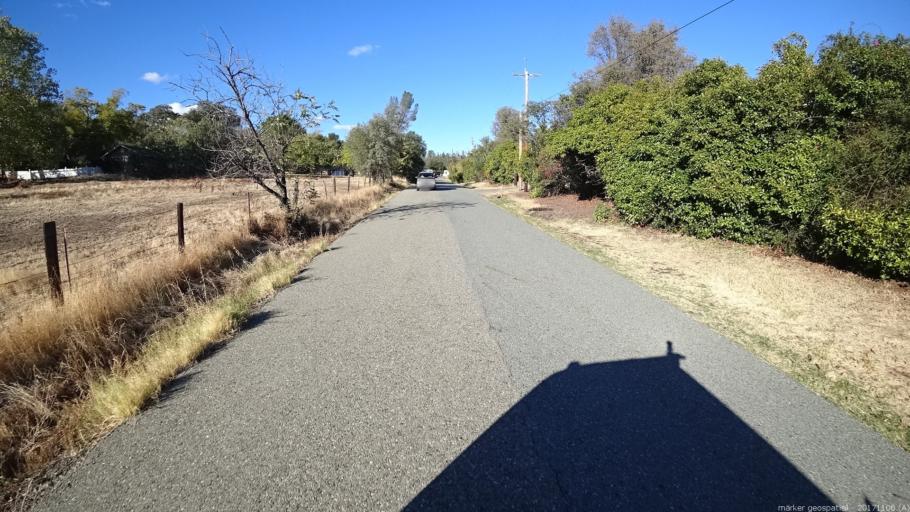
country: US
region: California
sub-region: Shasta County
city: Shasta
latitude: 40.5941
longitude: -122.4885
